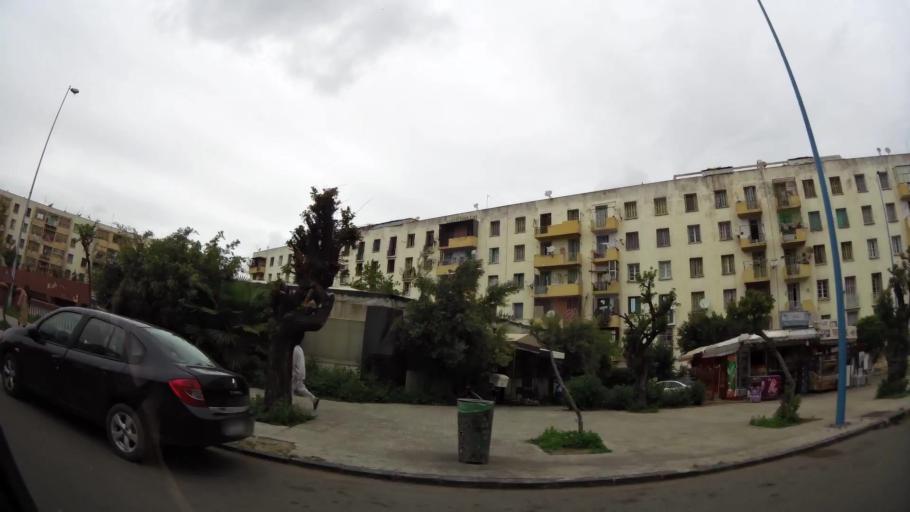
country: MA
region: Grand Casablanca
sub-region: Casablanca
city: Casablanca
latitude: 33.5717
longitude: -7.5557
